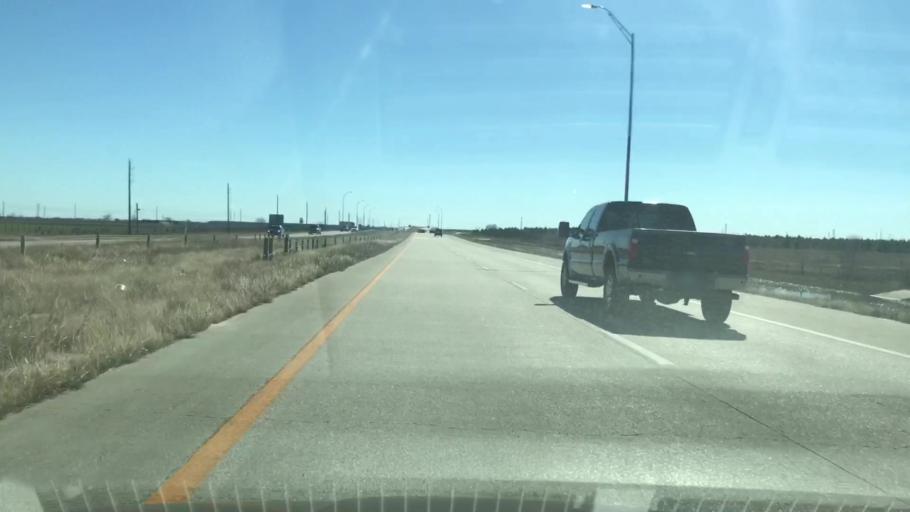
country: US
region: Texas
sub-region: Harris County
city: Cypress
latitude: 29.9325
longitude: -95.7635
